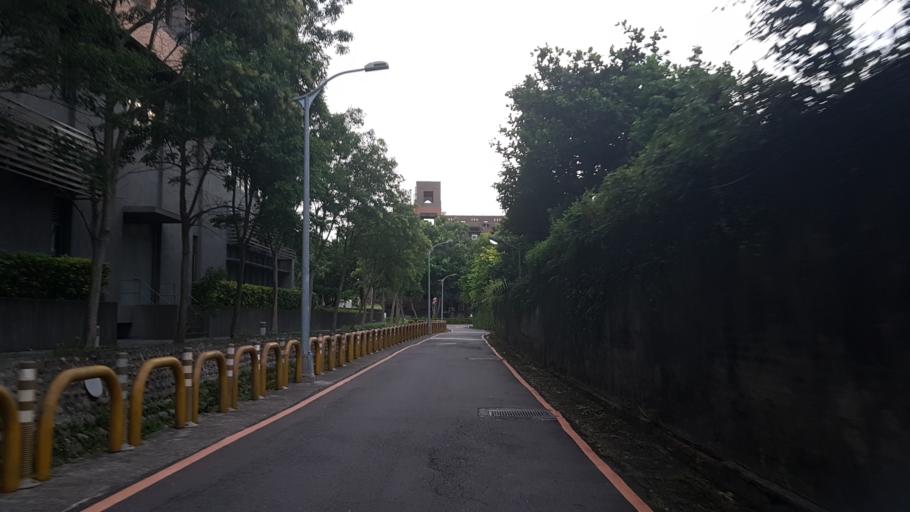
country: TW
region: Taipei
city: Taipei
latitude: 25.0137
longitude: 121.5477
